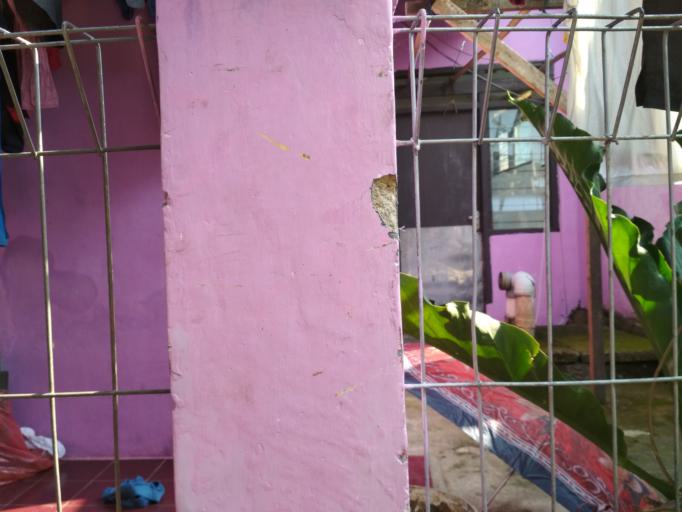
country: ID
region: West Java
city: Ciampea
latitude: -6.5615
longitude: 106.7338
